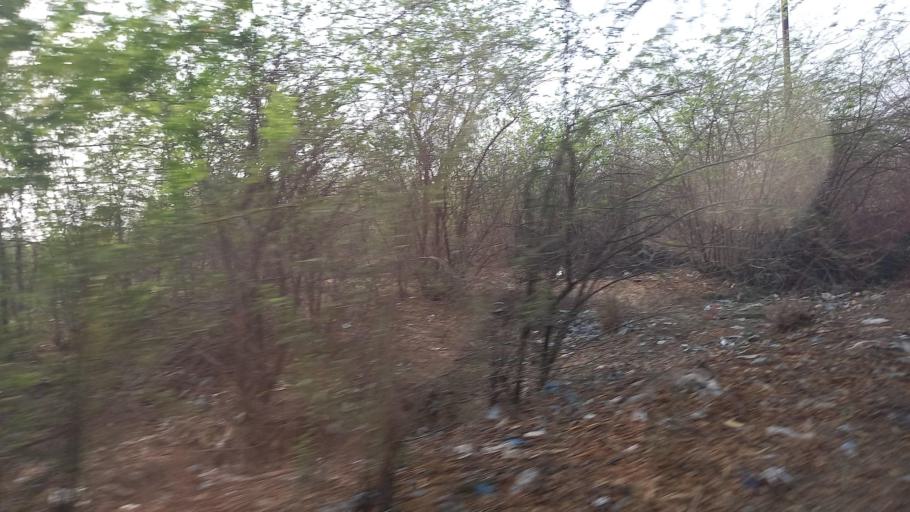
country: PK
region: Sindh
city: Malir Cantonment
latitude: 25.1162
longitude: 67.1916
